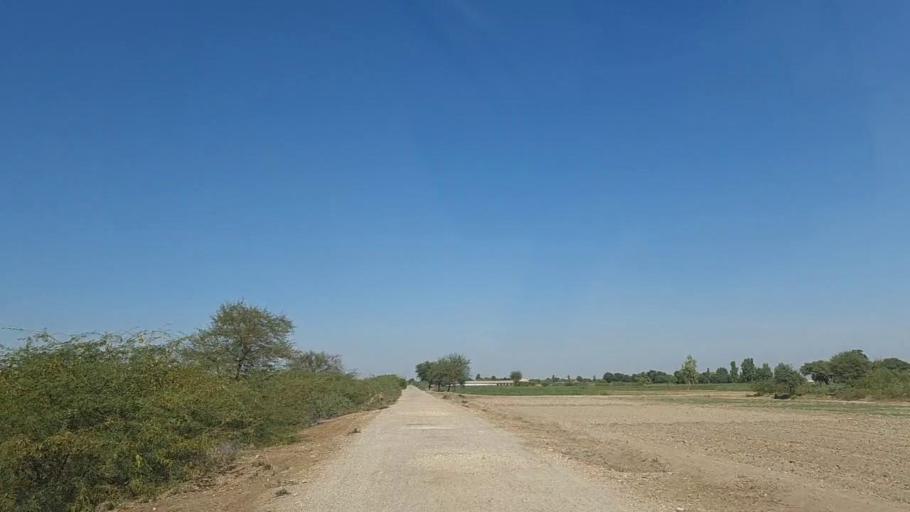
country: PK
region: Sindh
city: Samaro
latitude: 25.3030
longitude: 69.5148
